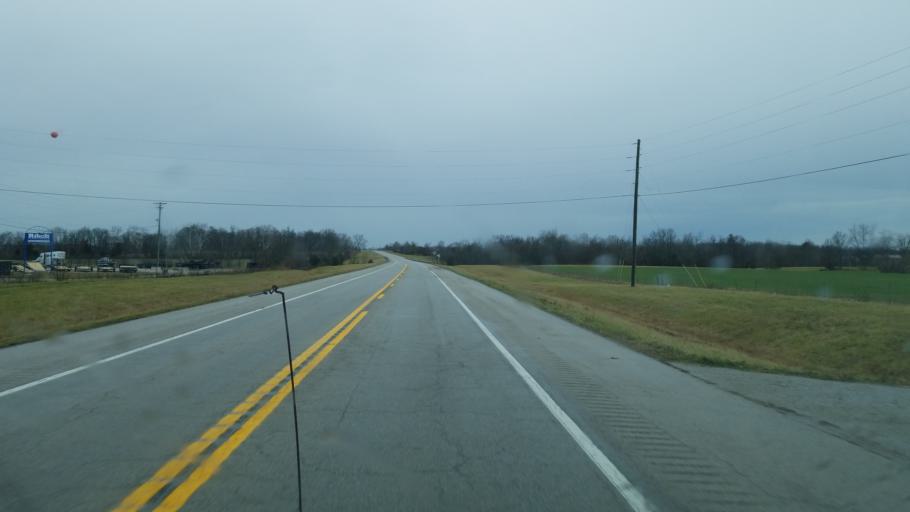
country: US
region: Ohio
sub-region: Adams County
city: Manchester
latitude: 38.5571
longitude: -83.5932
